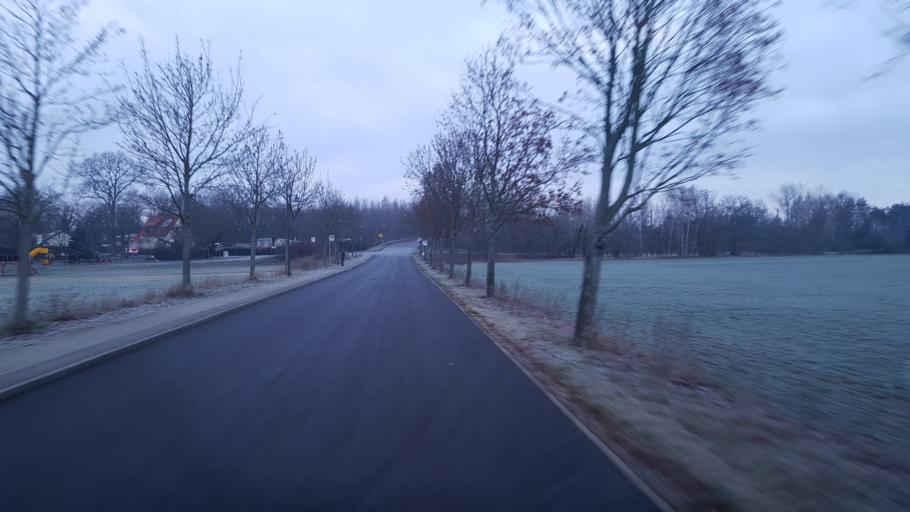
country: DE
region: Brandenburg
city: Ludwigsfelde
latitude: 52.3165
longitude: 13.2023
